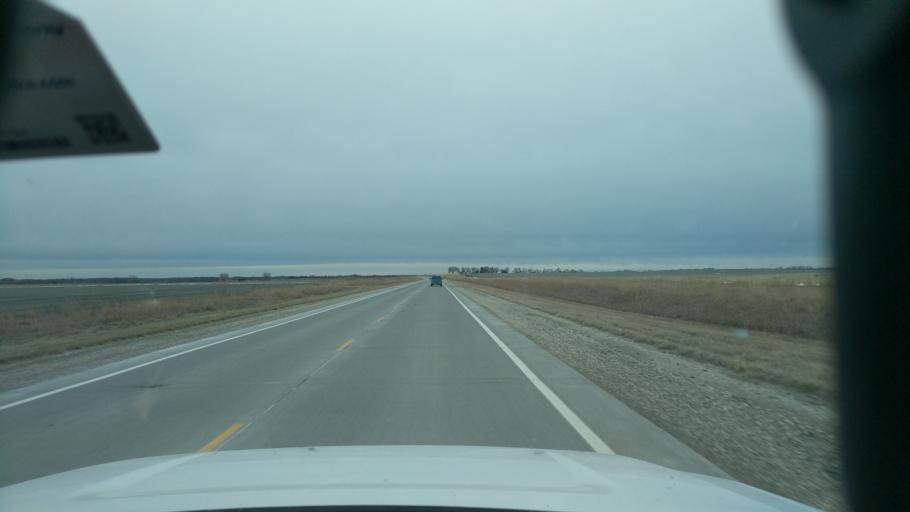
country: US
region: Kansas
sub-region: Dickinson County
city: Herington
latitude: 38.5479
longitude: -96.9575
